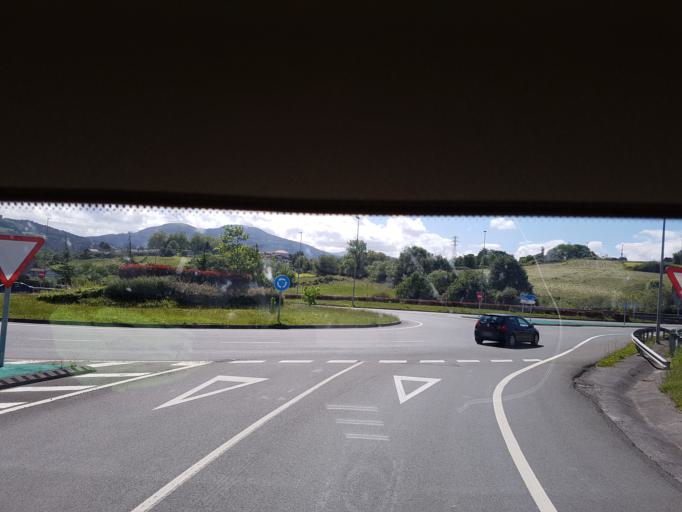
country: ES
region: Basque Country
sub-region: Bizkaia
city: San Julian de Muskiz
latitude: 43.3229
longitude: -3.0786
